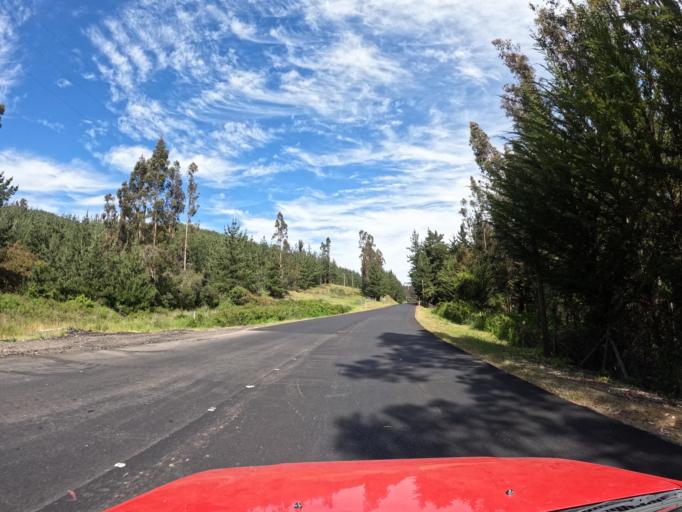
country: CL
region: Maule
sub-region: Provincia de Talca
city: Constitucion
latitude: -35.0447
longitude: -72.0517
